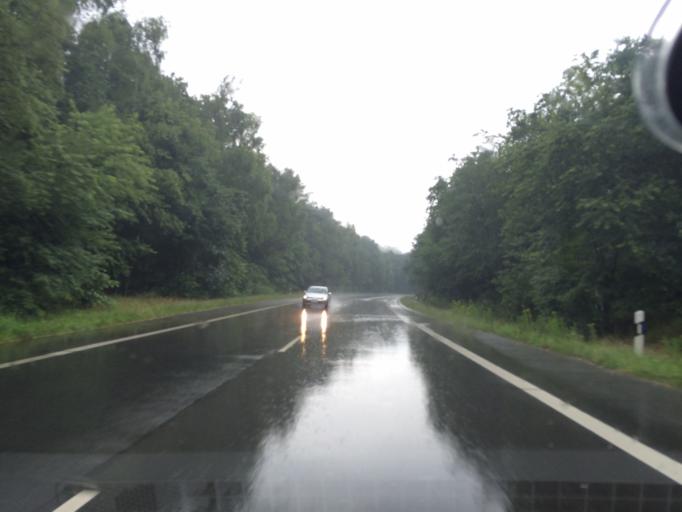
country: DE
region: North Rhine-Westphalia
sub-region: Regierungsbezirk Munster
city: Haltern
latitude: 51.7580
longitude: 7.2380
